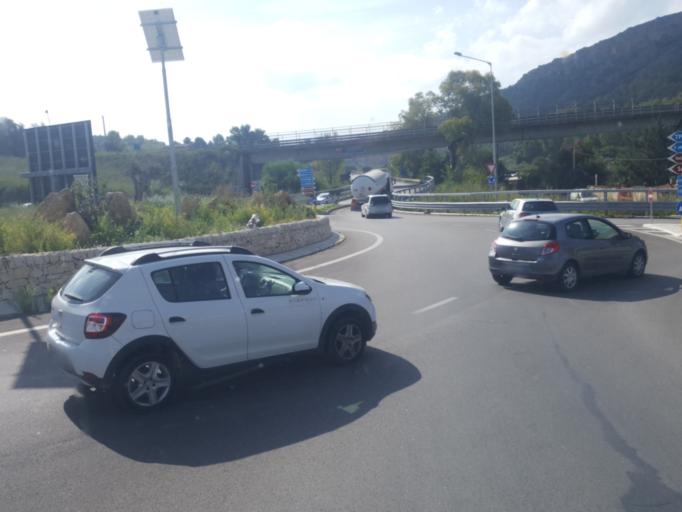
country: IT
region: Sicily
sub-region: Agrigento
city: Agrigento
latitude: 37.3096
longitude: 13.6081
